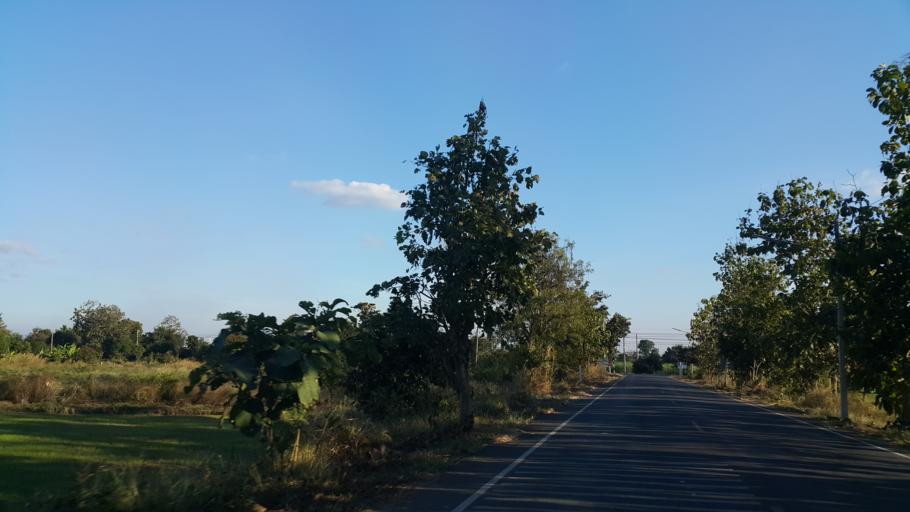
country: TH
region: Sukhothai
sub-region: Amphoe Si Satchanalai
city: Si Satchanalai
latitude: 17.5379
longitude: 99.7993
